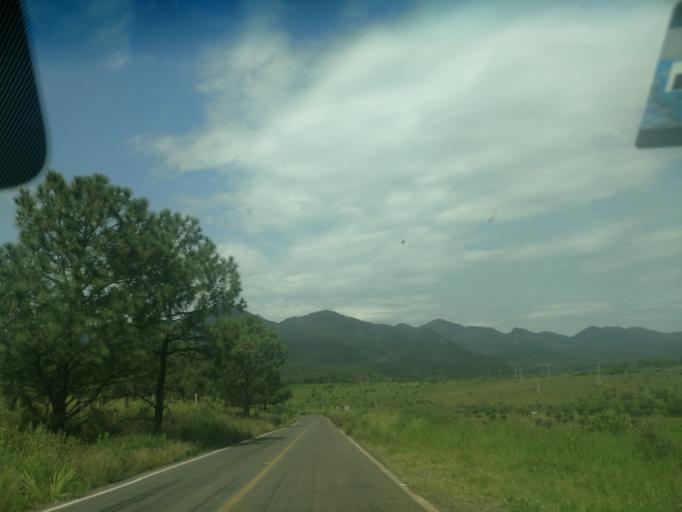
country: MX
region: Jalisco
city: Mascota
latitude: 20.4447
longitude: -104.7594
